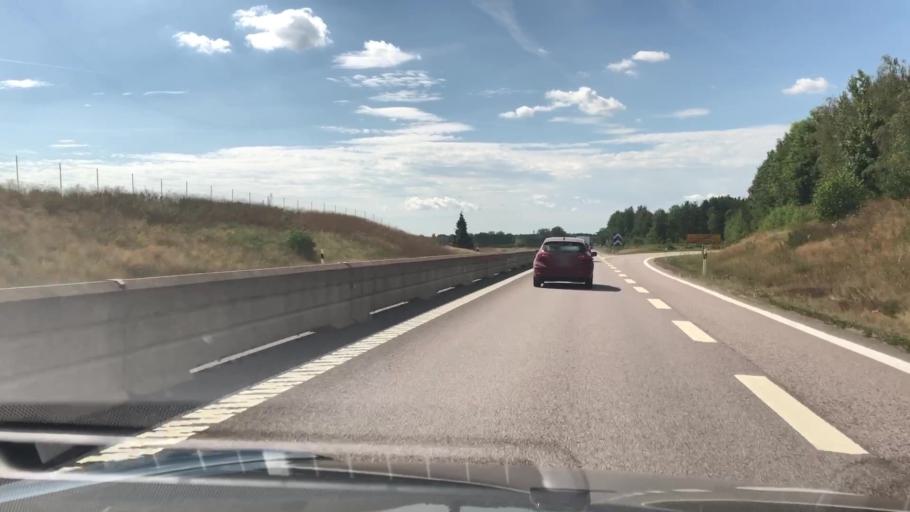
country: SE
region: Kalmar
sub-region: Kalmar Kommun
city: Ljungbyholm
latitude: 56.5911
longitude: 16.1226
